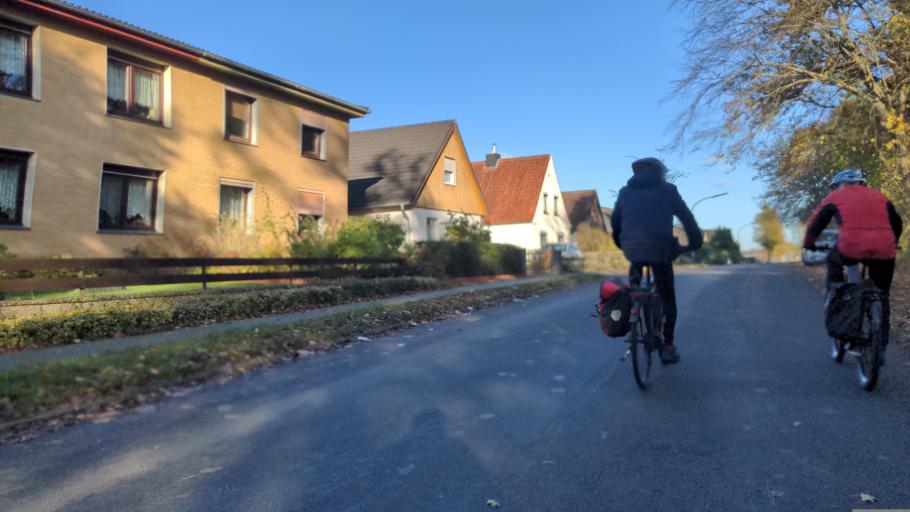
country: DE
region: Schleswig-Holstein
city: Ratekau
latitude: 53.9379
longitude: 10.7250
